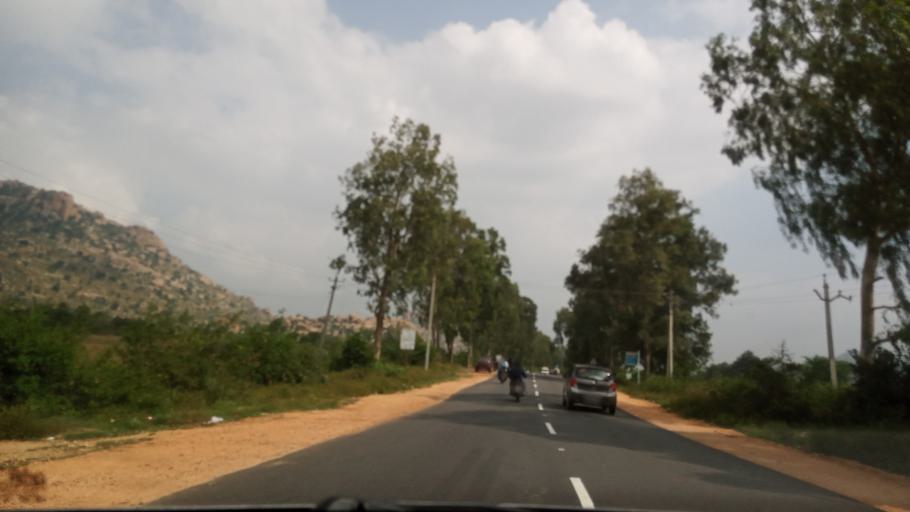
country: IN
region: Andhra Pradesh
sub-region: Chittoor
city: Madanapalle
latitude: 13.6360
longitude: 78.6013
